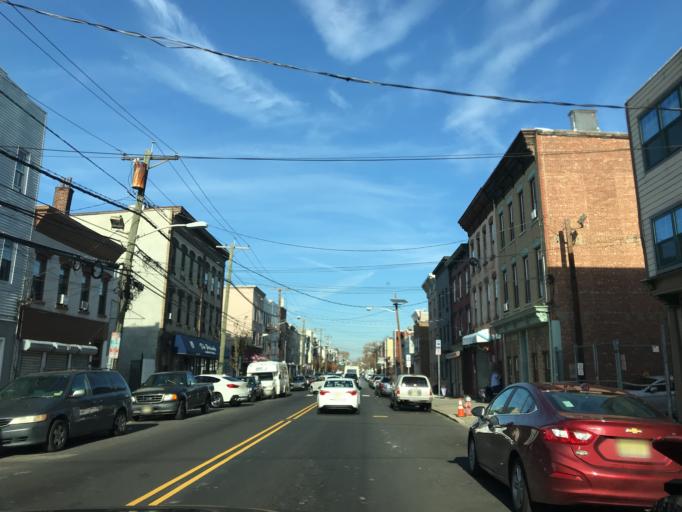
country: US
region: New Jersey
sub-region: Hudson County
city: Hoboken
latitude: 40.7421
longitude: -74.0456
